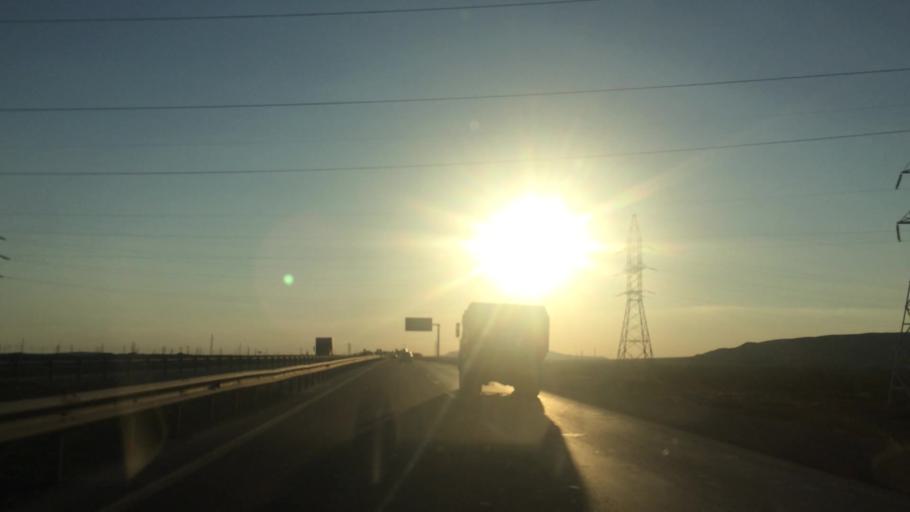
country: AZ
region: Baki
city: Qobustan
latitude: 39.9627
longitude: 49.3987
